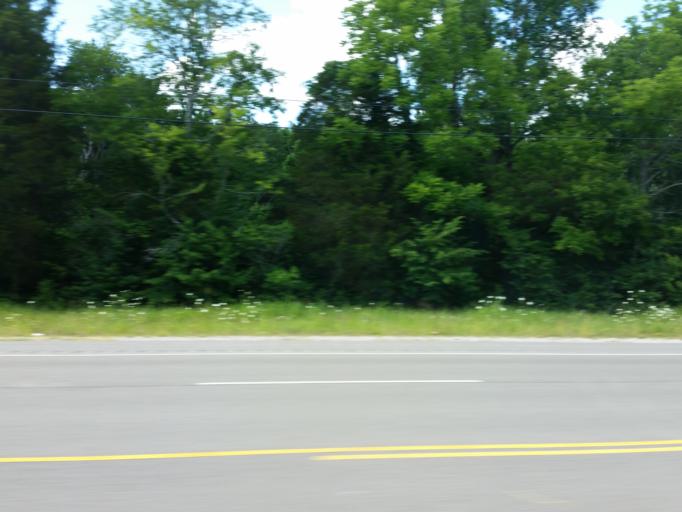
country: US
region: Tennessee
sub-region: Lewis County
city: Hohenwald
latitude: 35.5677
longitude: -87.4177
